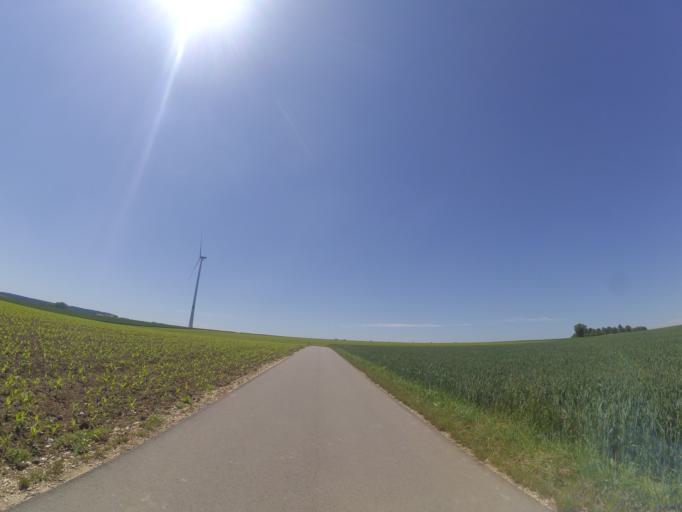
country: DE
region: Baden-Wuerttemberg
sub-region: Tuebingen Region
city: Dornstadt
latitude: 48.4746
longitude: 9.8537
